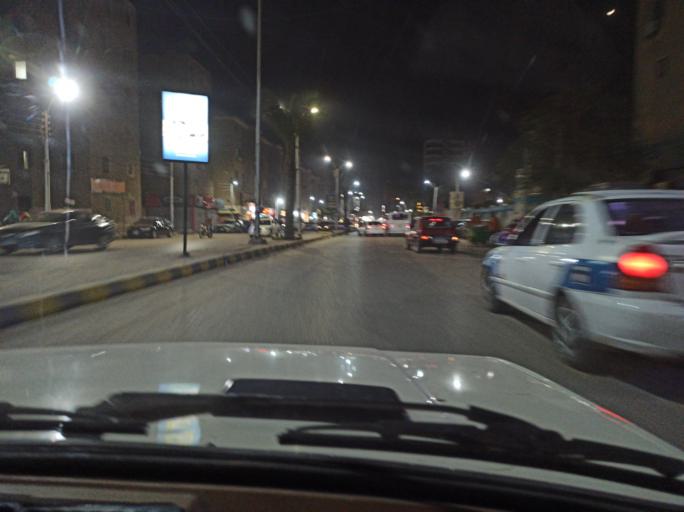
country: EG
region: Muhafazat Bani Suwayf
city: Bani Suwayf
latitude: 29.0716
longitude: 31.1075
